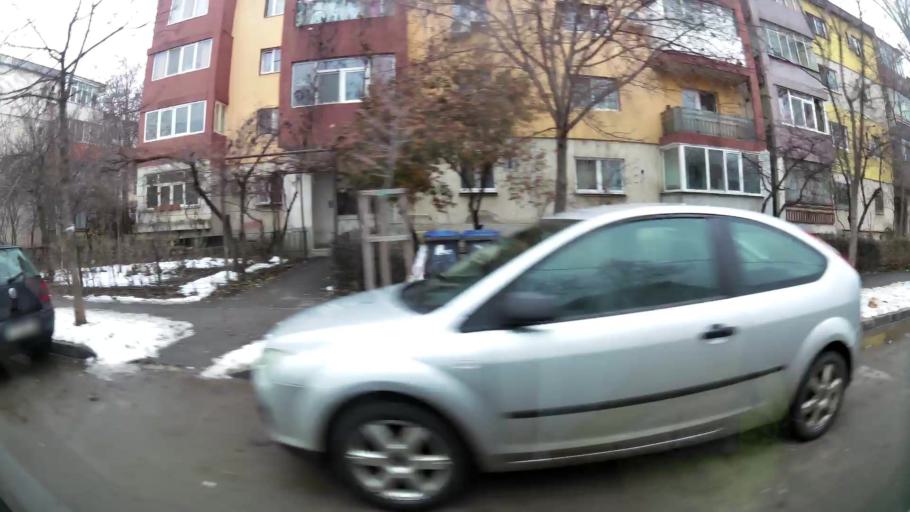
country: RO
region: Ilfov
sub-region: Comuna Chiajna
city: Rosu
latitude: 44.4375
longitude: 26.0058
